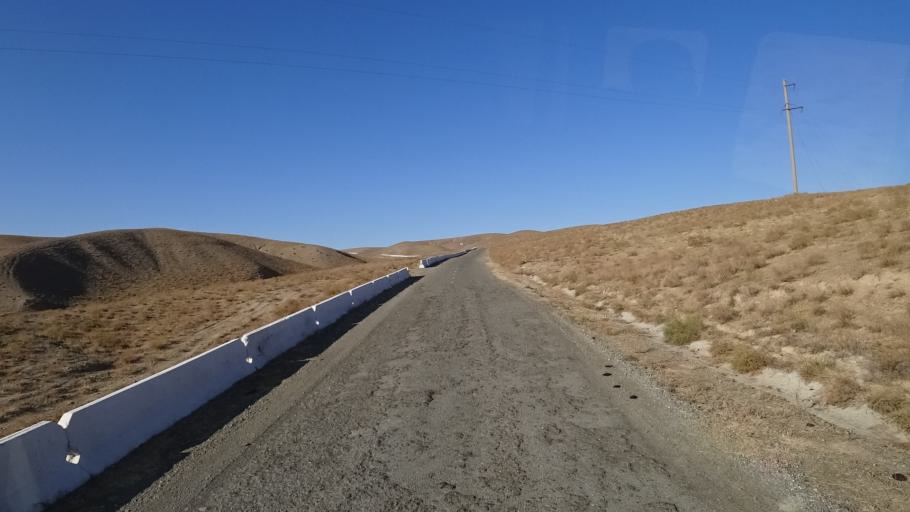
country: UZ
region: Navoiy
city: Karmana Shahri
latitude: 40.2734
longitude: 65.5773
